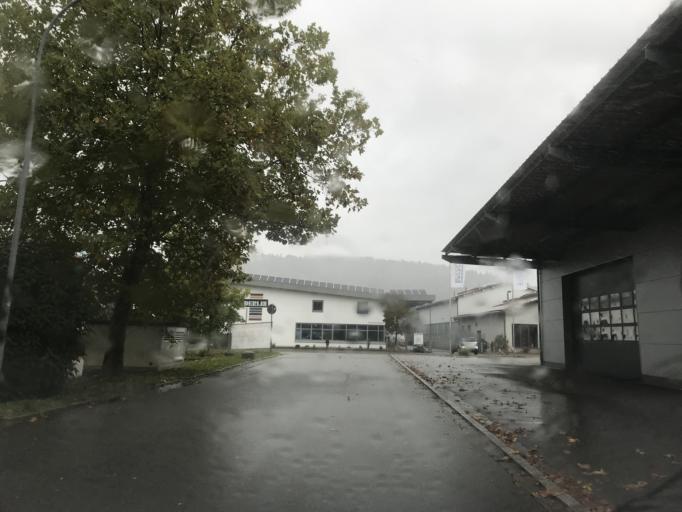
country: DE
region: Baden-Wuerttemberg
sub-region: Freiburg Region
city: Schopfheim
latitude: 47.6429
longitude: 7.8115
